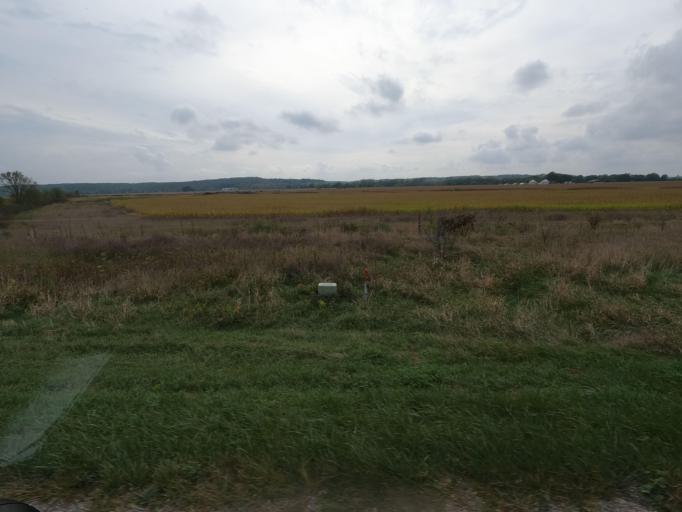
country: US
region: Iowa
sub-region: Wapello County
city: Ottumwa
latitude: 40.9060
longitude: -92.2031
